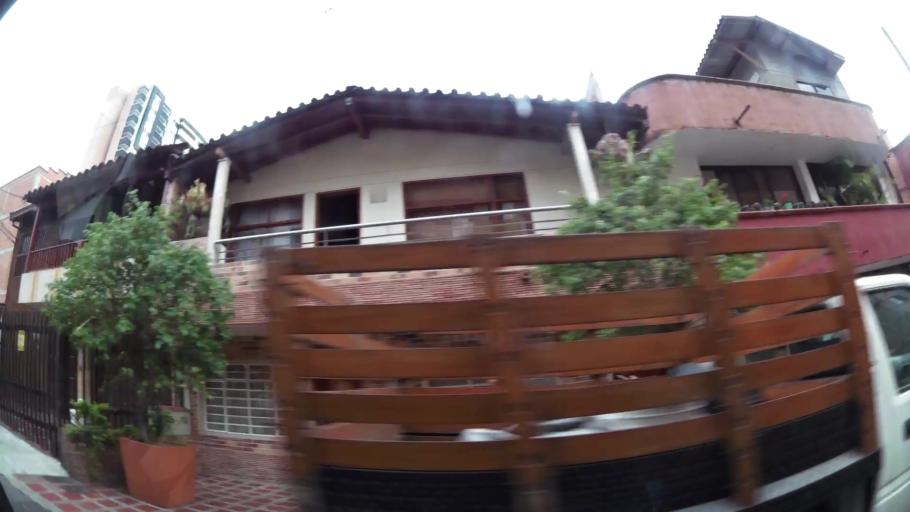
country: CO
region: Antioquia
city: Envigado
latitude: 6.1607
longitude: -75.5948
